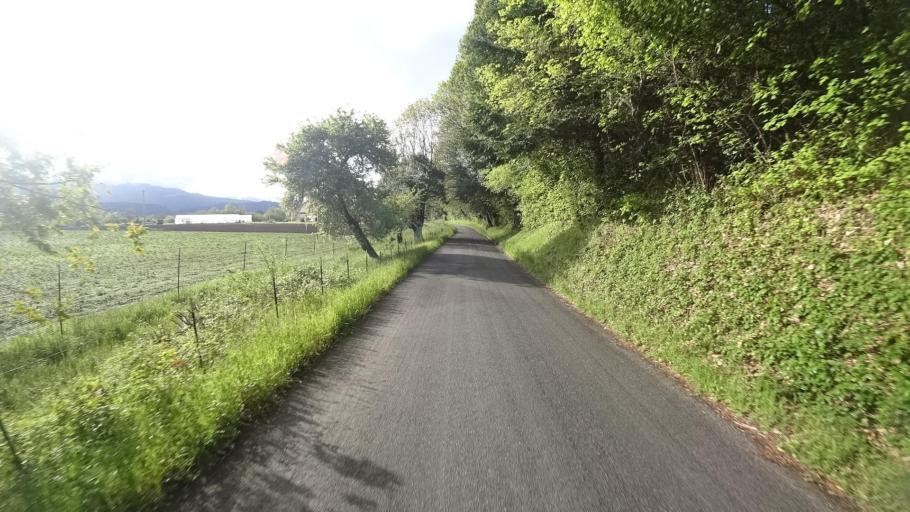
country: US
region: California
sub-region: Humboldt County
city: Blue Lake
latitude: 40.8791
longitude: -124.0147
